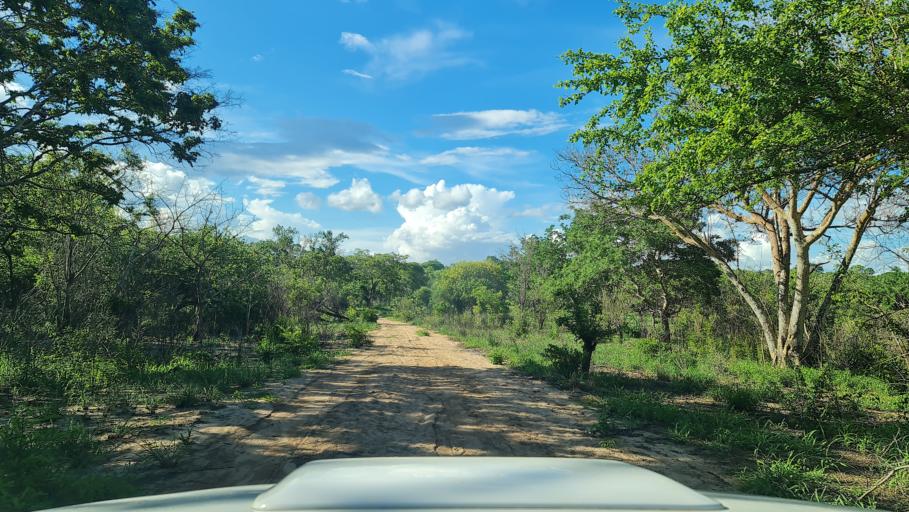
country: MZ
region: Nampula
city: Ilha de Mocambique
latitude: -15.2567
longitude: 40.1833
